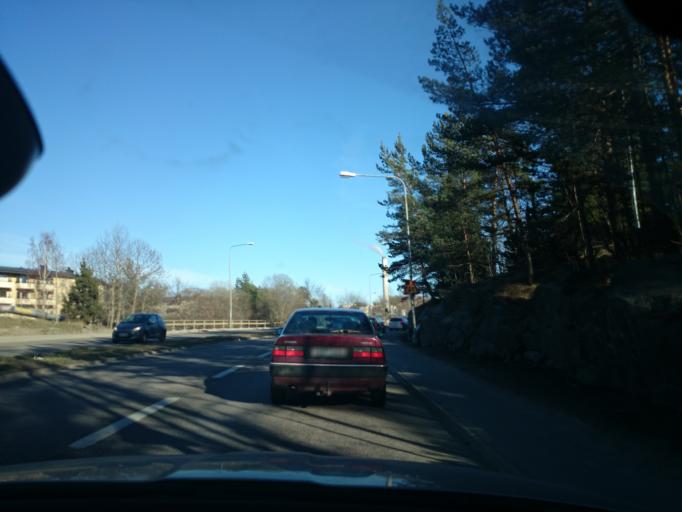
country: SE
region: Stockholm
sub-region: Stockholms Kommun
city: Arsta
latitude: 59.2597
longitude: 18.0432
